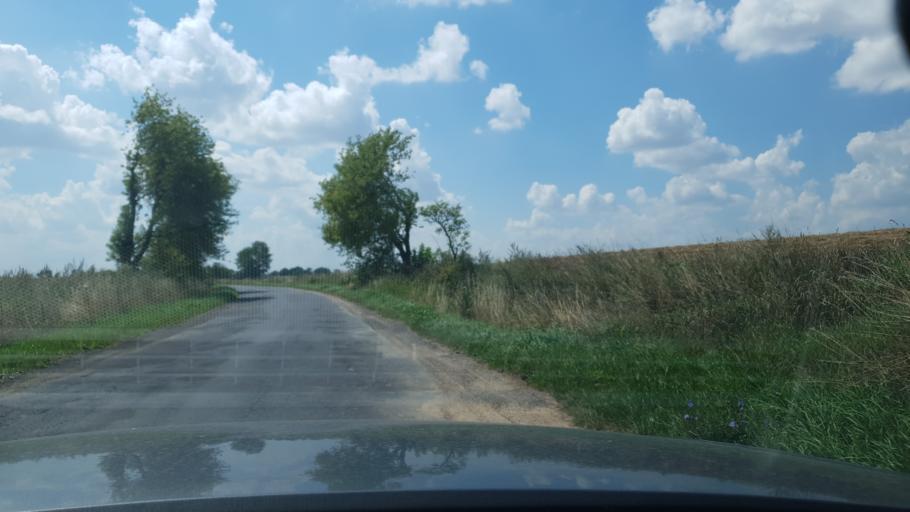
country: PL
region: Kujawsko-Pomorskie
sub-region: Powiat wabrzeski
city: Pluznica
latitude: 53.3024
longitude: 18.8070
